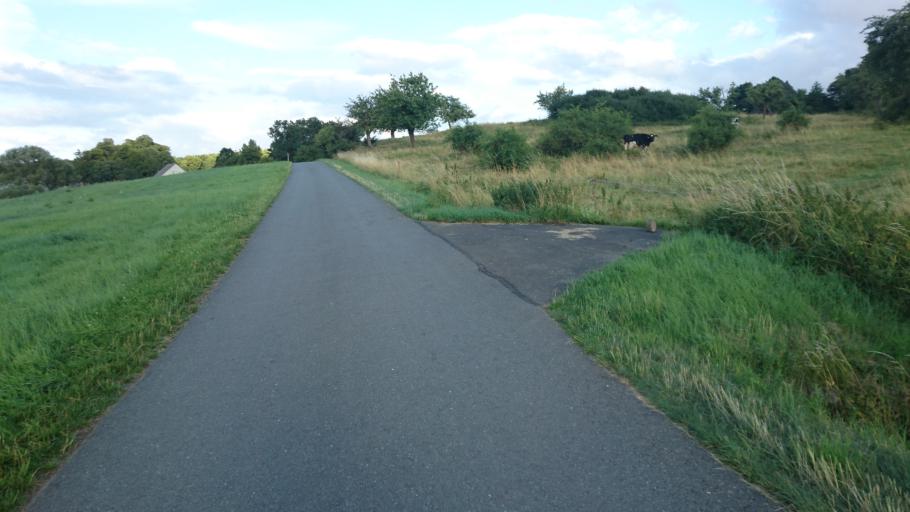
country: DE
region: Thuringia
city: Schleiz
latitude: 50.5569
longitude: 11.8013
